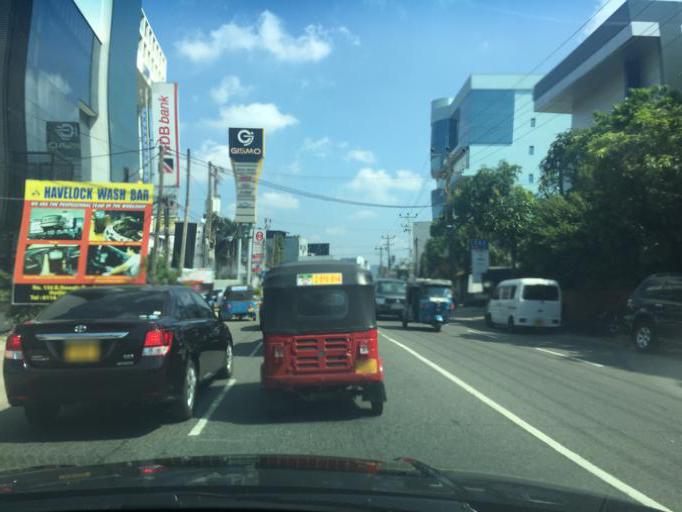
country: LK
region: Western
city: Pita Kotte
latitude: 6.8822
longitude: 79.8888
